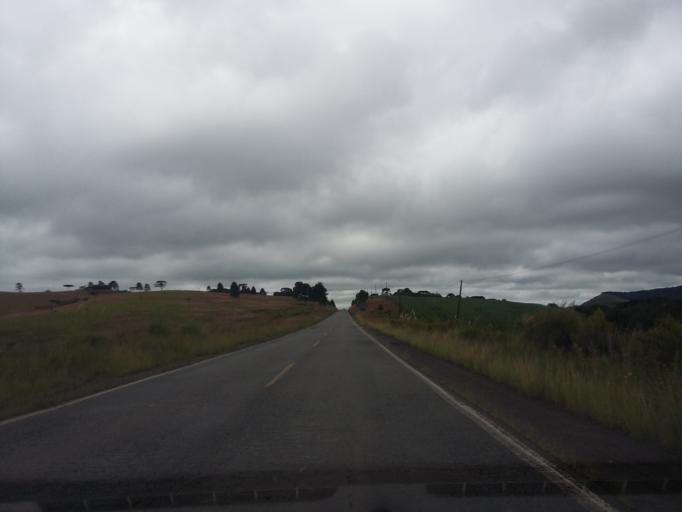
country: BR
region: Santa Catarina
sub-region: Lages
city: Lages
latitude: -27.8416
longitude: -50.2317
